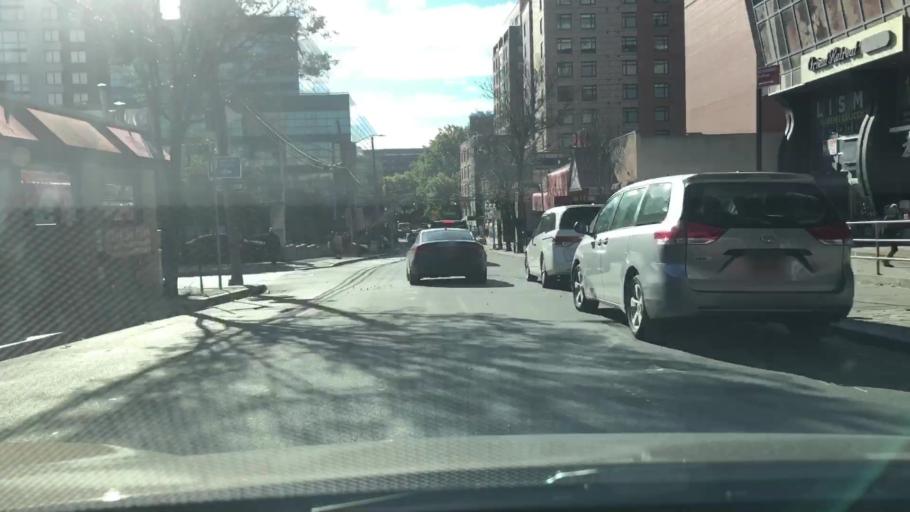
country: US
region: New York
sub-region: Queens County
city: Jamaica
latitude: 40.7604
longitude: -73.8327
